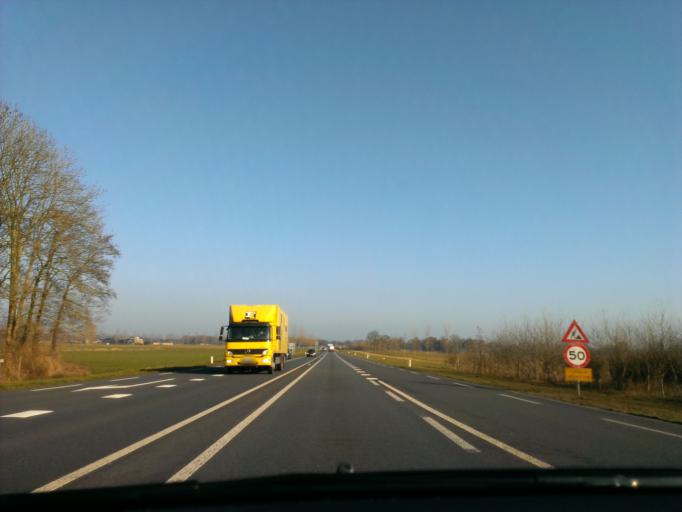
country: NL
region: Overijssel
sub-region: Gemeente Hof van Twente
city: Goor
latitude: 52.2979
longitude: 6.5538
